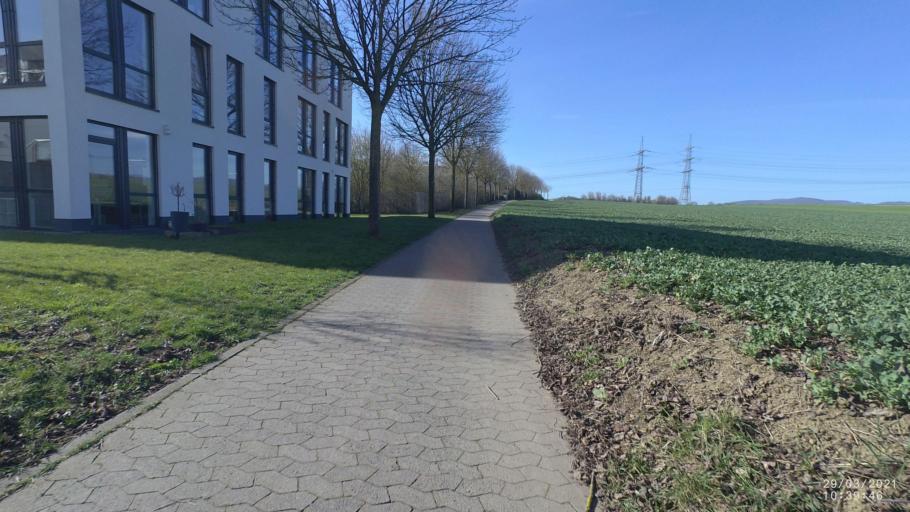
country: DE
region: Rheinland-Pfalz
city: Leutesdorf
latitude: 50.4284
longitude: 7.3791
